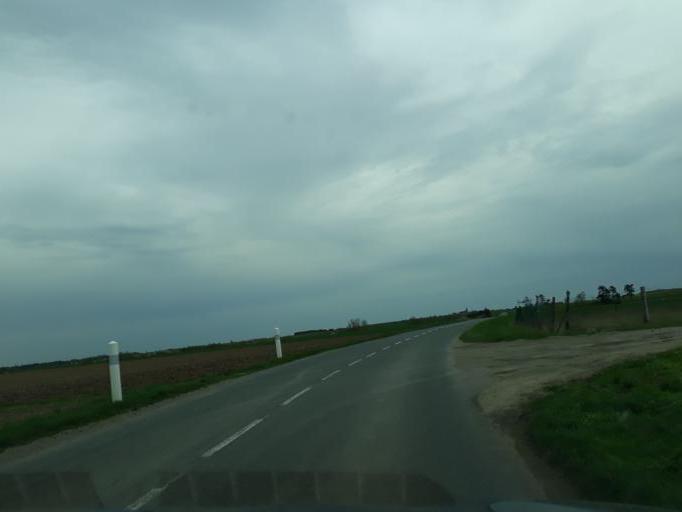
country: FR
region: Centre
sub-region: Departement du Loiret
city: Epieds-en-Beauce
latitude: 47.9104
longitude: 1.6106
